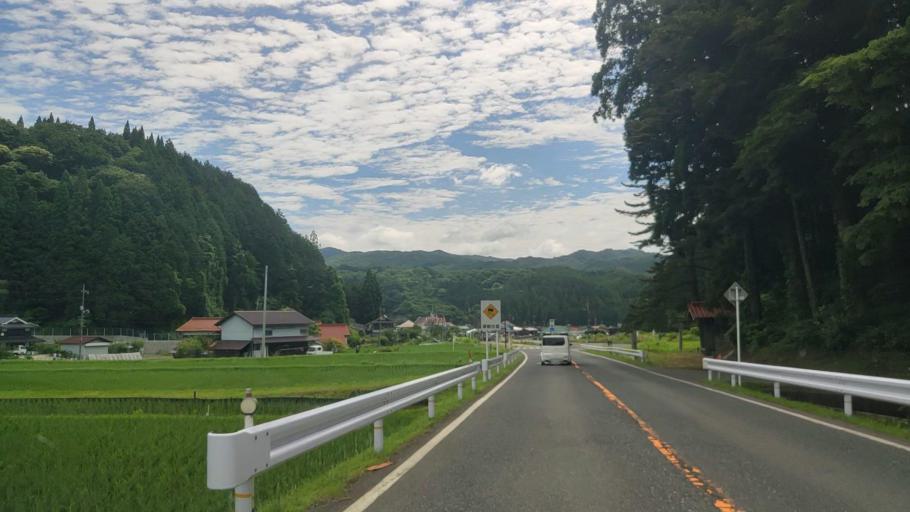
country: JP
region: Okayama
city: Niimi
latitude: 35.1782
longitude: 133.5615
